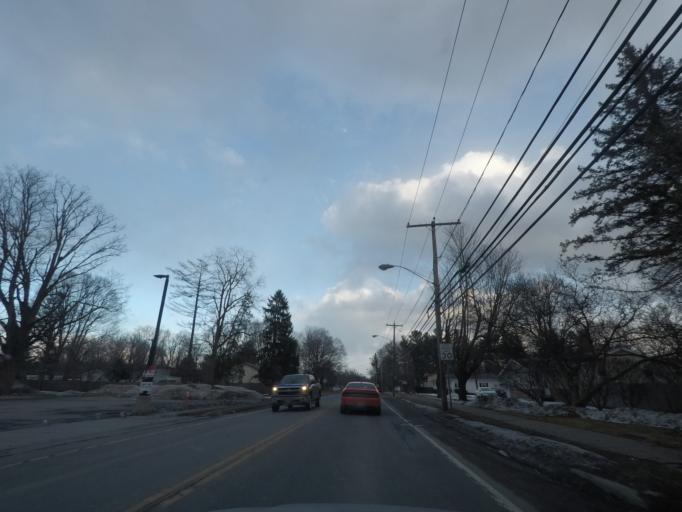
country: US
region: New York
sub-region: Oneida County
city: Utica
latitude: 43.1100
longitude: -75.1804
